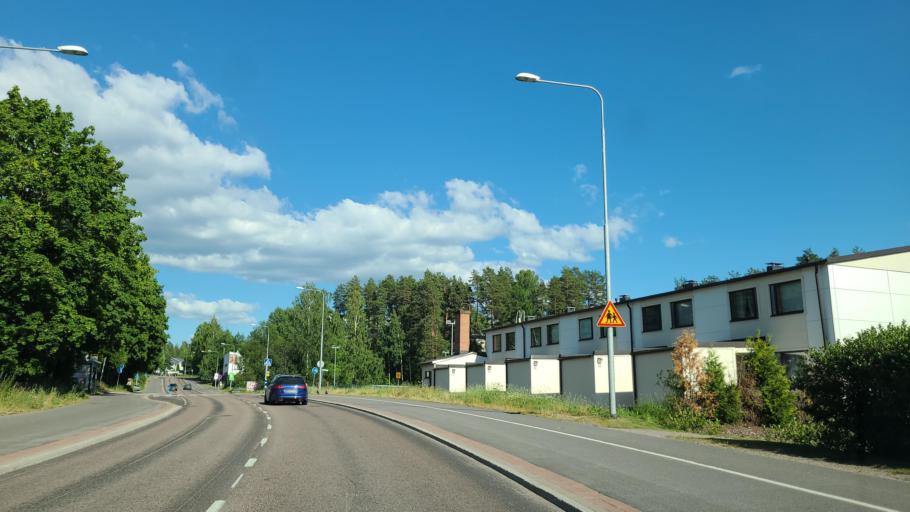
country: FI
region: Central Finland
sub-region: Jyvaeskylae
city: Jyvaeskylae
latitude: 62.2432
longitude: 25.7911
